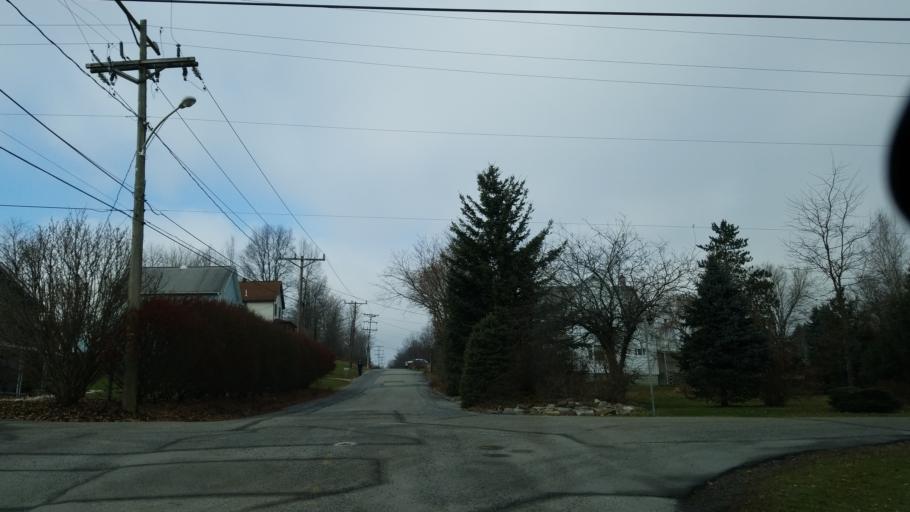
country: US
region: Pennsylvania
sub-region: Clearfield County
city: Sandy
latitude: 41.1274
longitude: -78.7815
